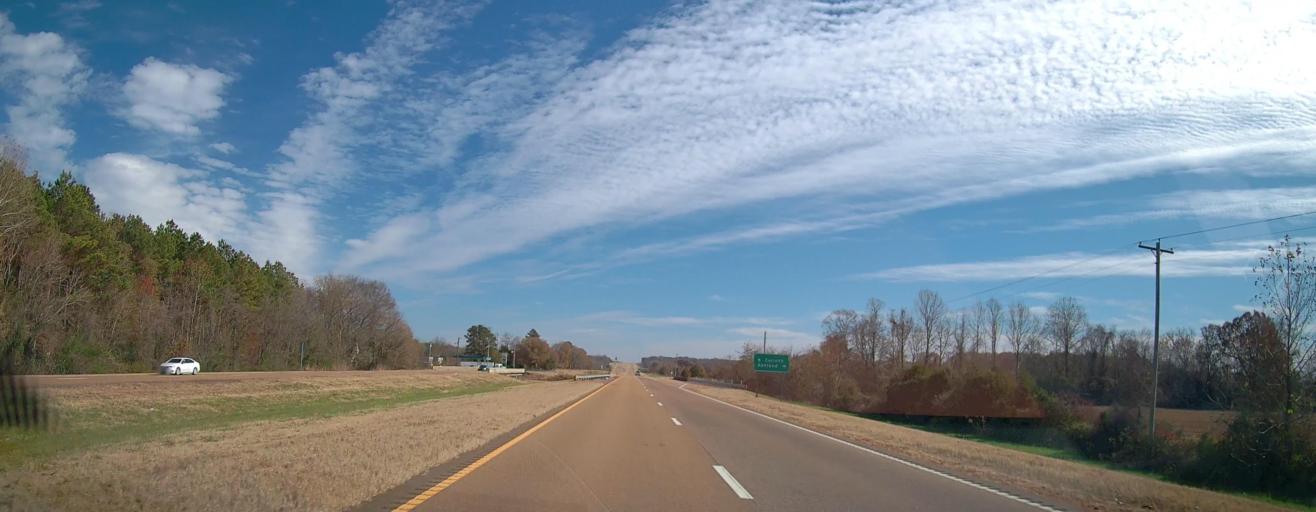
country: US
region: Mississippi
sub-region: Benton County
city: Ashland
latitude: 34.9462
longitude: -89.2141
